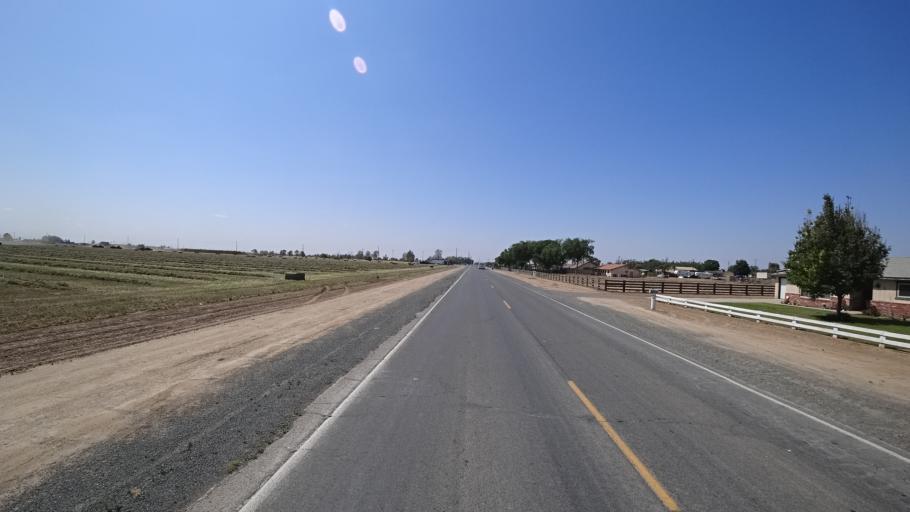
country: US
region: California
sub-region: Kings County
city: Home Garden
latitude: 36.3169
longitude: -119.6190
